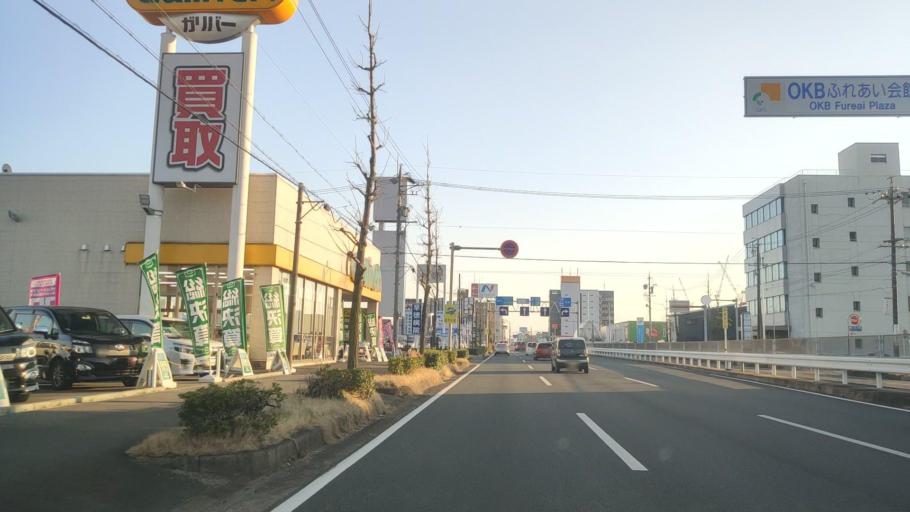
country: JP
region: Gifu
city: Gifu-shi
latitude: 35.3974
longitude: 136.7265
